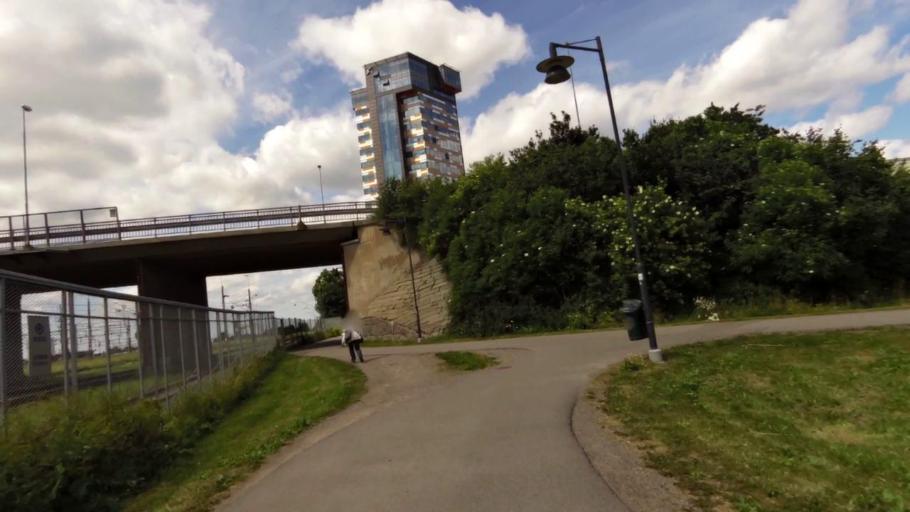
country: SE
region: OEstergoetland
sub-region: Linkopings Kommun
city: Linkoping
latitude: 58.4212
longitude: 15.6181
